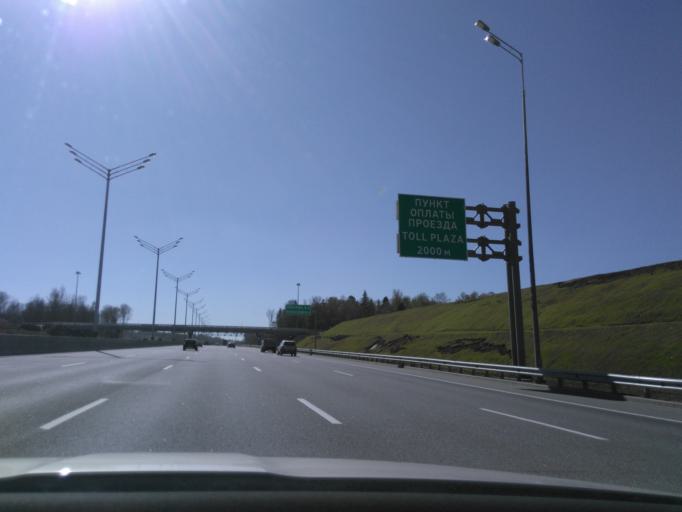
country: RU
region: Moscow
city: Khimki
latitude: 55.9509
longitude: 37.4348
